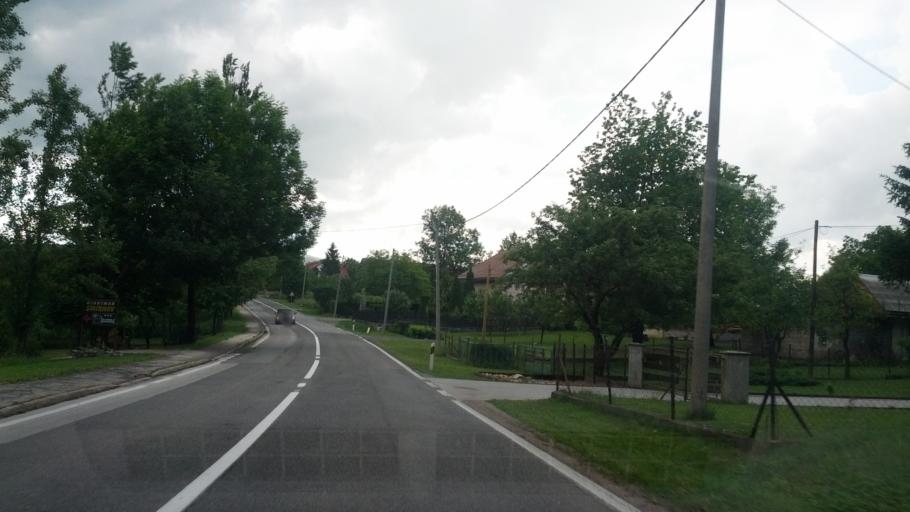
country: HR
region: Licko-Senjska
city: Jezerce
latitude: 44.9547
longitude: 15.6708
